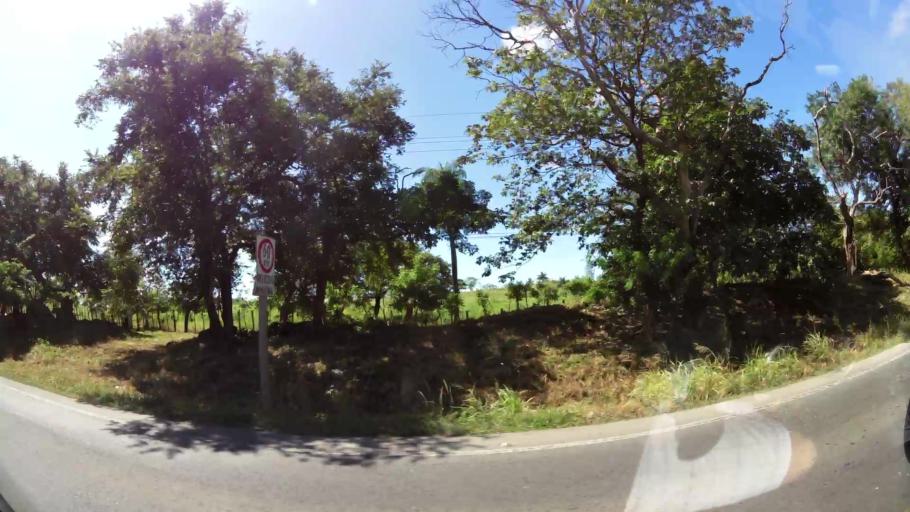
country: CR
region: Guanacaste
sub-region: Canton de Canas
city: Canas
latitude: 10.4037
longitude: -85.0848
